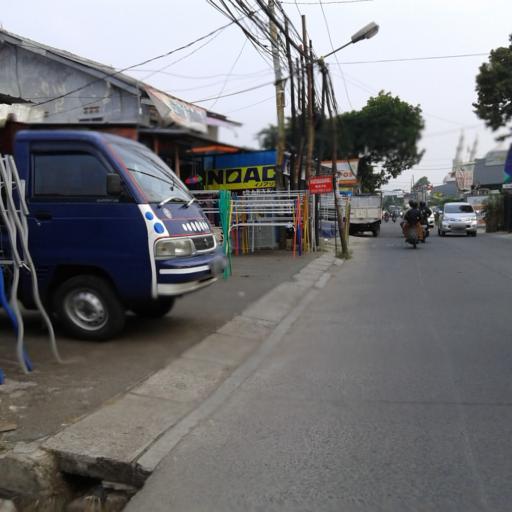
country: ID
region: West Java
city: Sawangan
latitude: -6.3911
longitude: 106.7692
